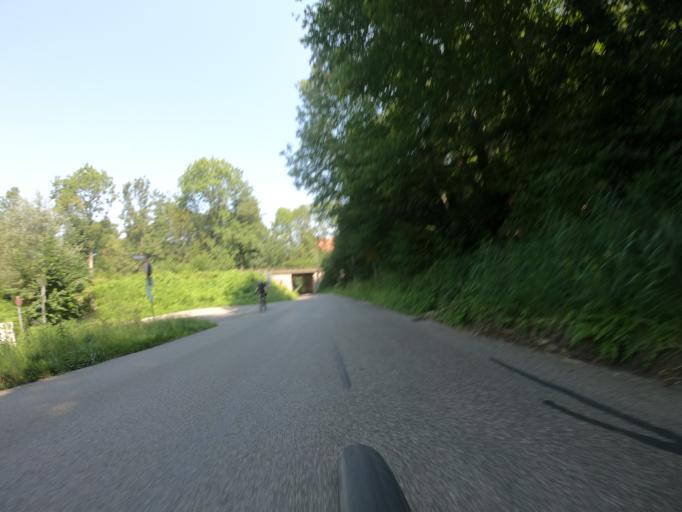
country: DE
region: Bavaria
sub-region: Upper Bavaria
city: Fuerstenfeldbruck
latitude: 48.1674
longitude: 11.2483
